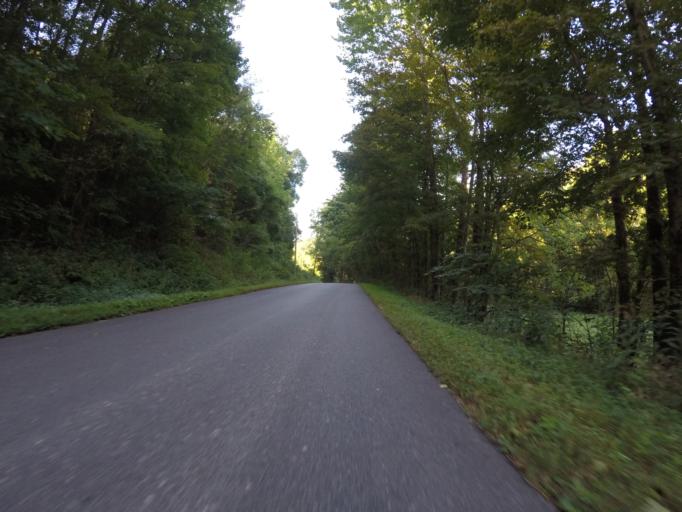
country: US
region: Ohio
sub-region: Lawrence County
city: Coal Grove
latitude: 38.5608
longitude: -82.5512
